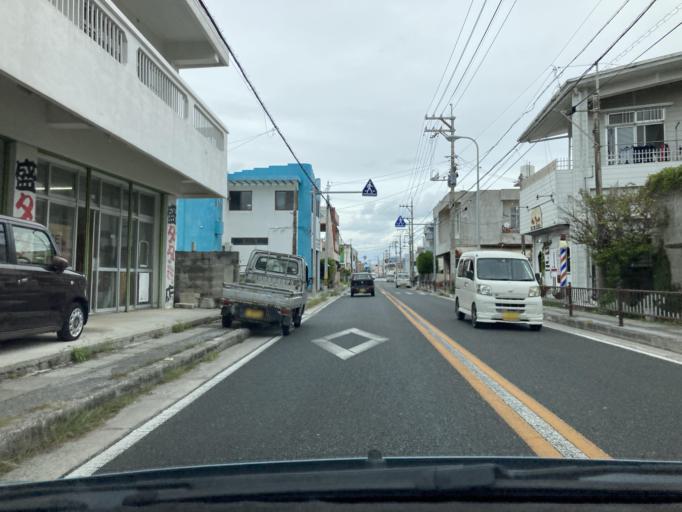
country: JP
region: Okinawa
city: Itoman
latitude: 26.1239
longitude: 127.6699
